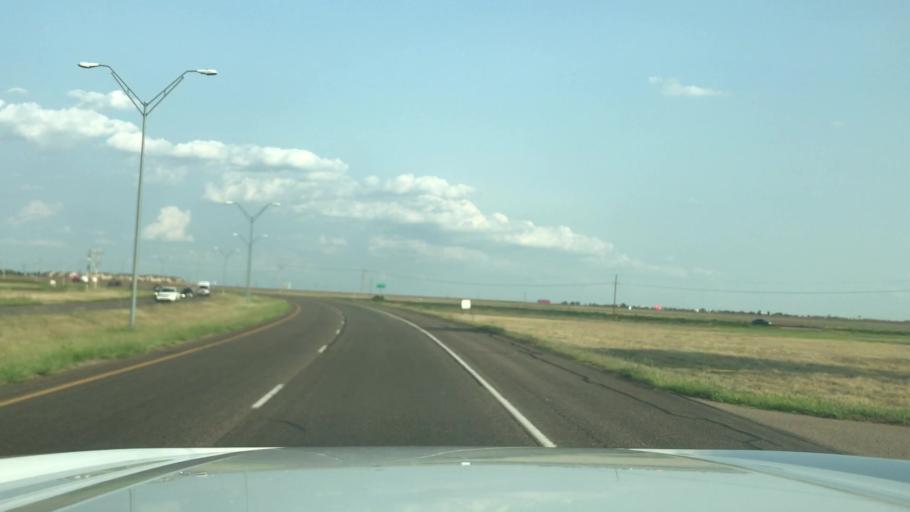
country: US
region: Texas
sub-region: Randall County
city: Canyon
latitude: 35.1189
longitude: -101.9358
